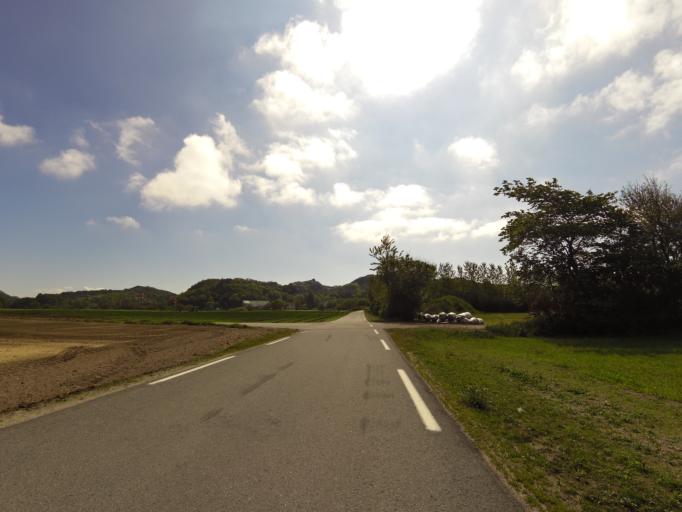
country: NO
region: Rogaland
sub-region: Ha
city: Vigrestad
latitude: 58.5183
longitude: 5.8175
